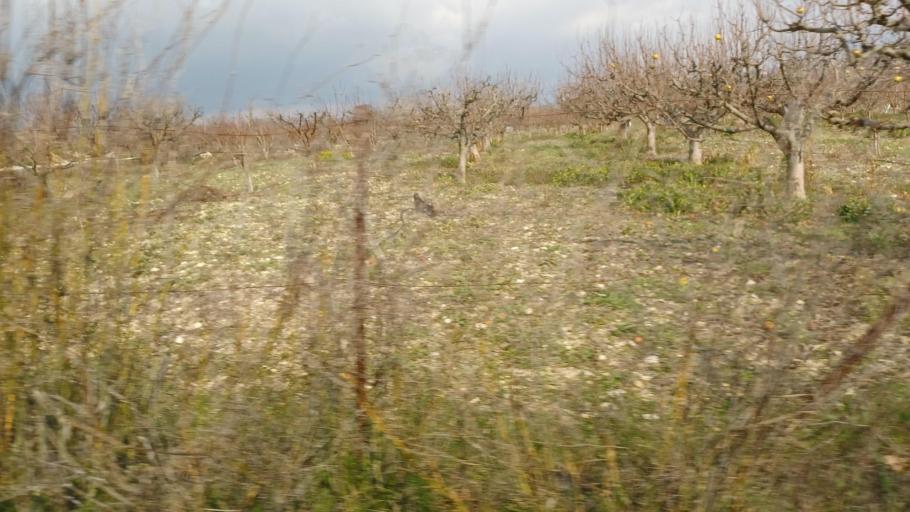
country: CY
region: Pafos
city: Tala
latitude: 34.8805
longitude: 32.4858
